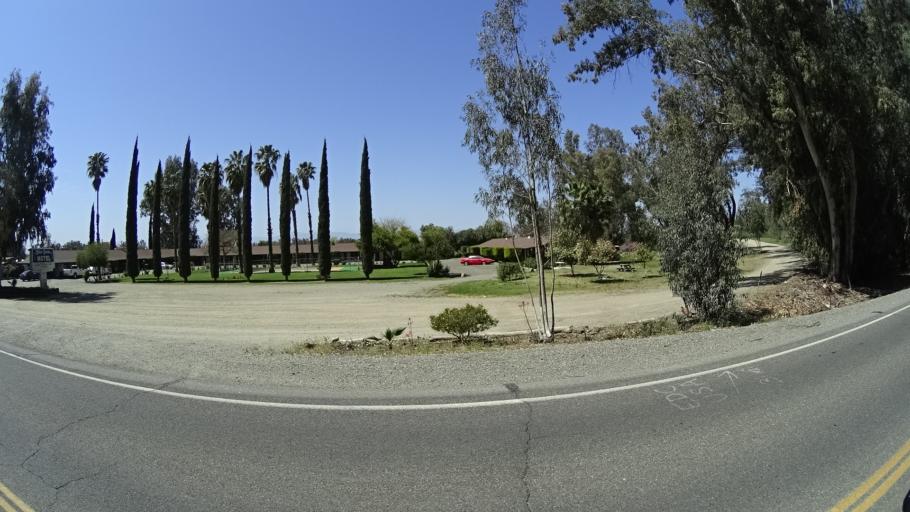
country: US
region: California
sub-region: Glenn County
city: Willows
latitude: 39.5946
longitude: -122.1946
